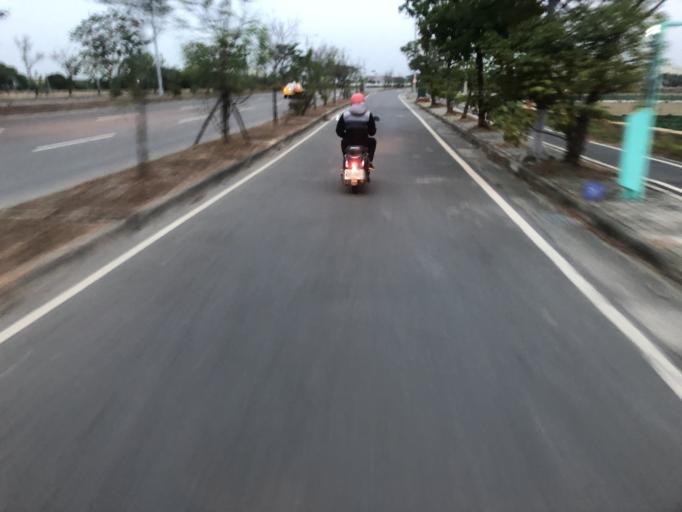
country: TW
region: Taiwan
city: Yujing
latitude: 23.1099
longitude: 120.3117
